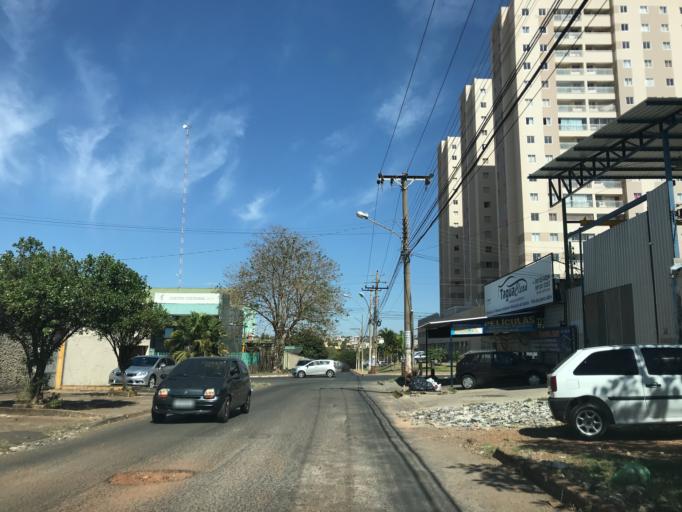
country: BR
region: Federal District
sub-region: Brasilia
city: Brasilia
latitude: -15.8119
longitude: -48.0719
